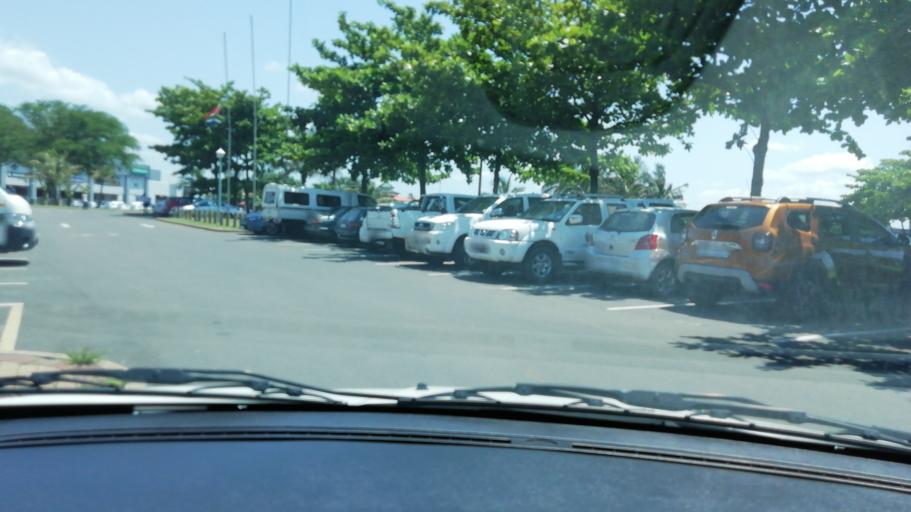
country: ZA
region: KwaZulu-Natal
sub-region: uThungulu District Municipality
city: Richards Bay
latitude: -28.7558
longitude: 32.0509
